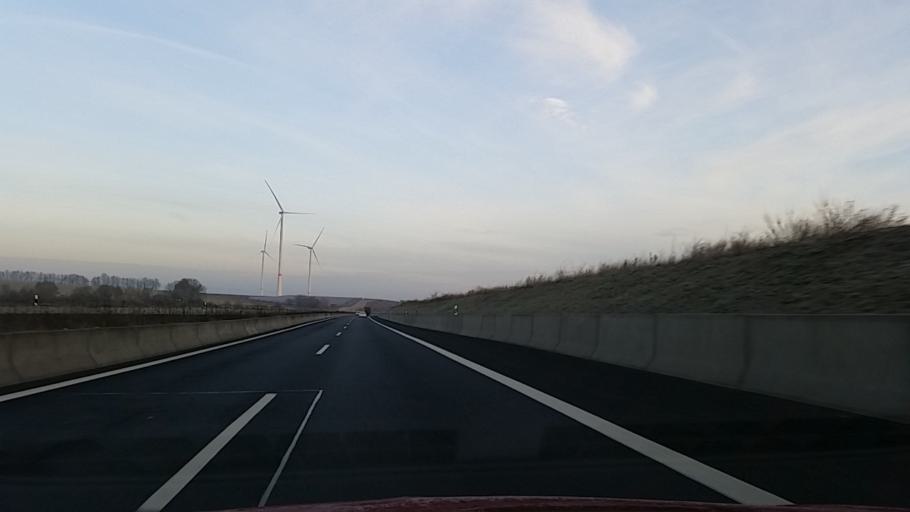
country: DE
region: Bavaria
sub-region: Regierungsbezirk Unterfranken
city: Munnerstadt
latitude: 50.2156
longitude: 10.2194
